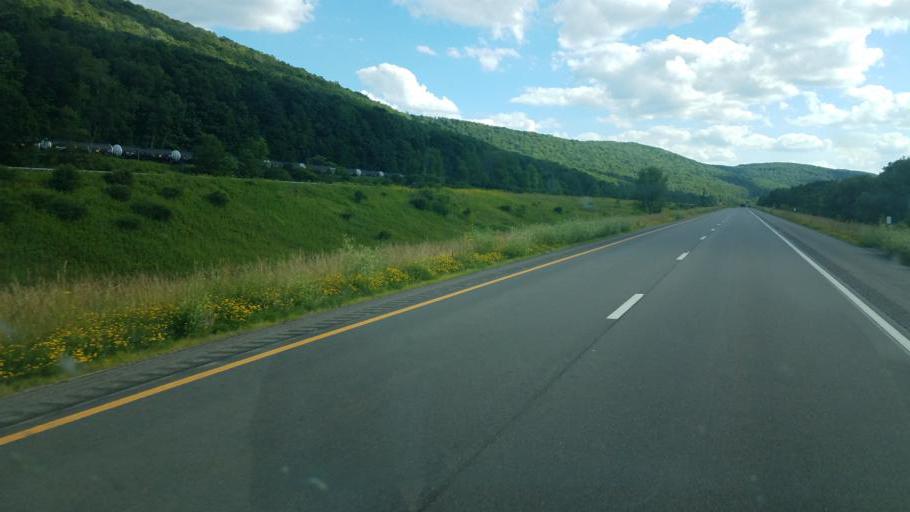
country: US
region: New York
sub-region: Allegany County
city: Cuba
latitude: 42.2063
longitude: -78.3273
